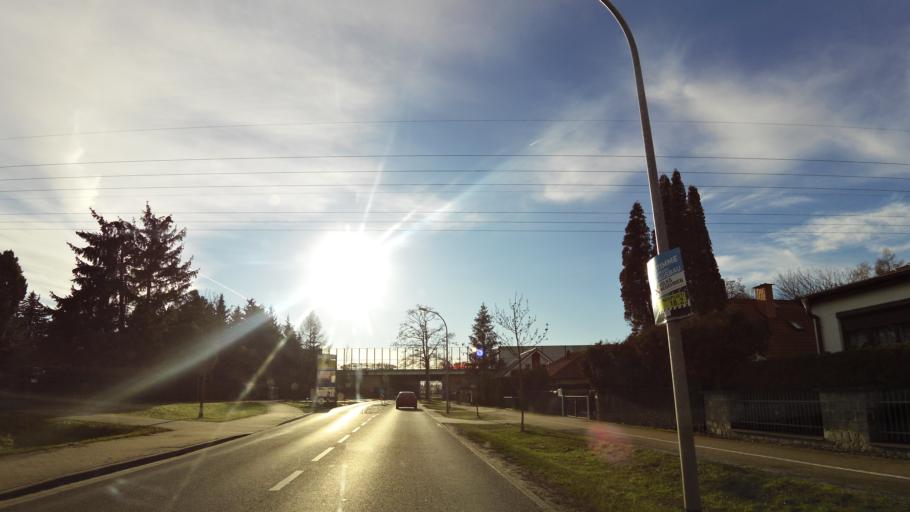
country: DE
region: Brandenburg
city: Petershagen
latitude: 52.5087
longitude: 13.7382
